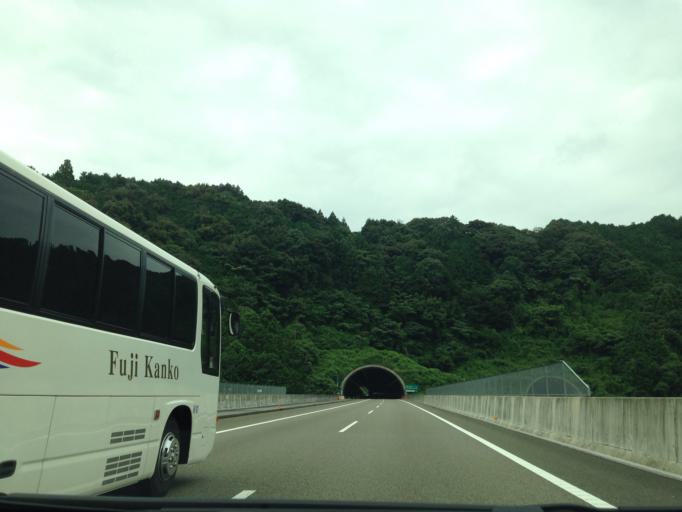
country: JP
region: Shizuoka
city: Shimada
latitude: 34.8724
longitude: 138.1702
